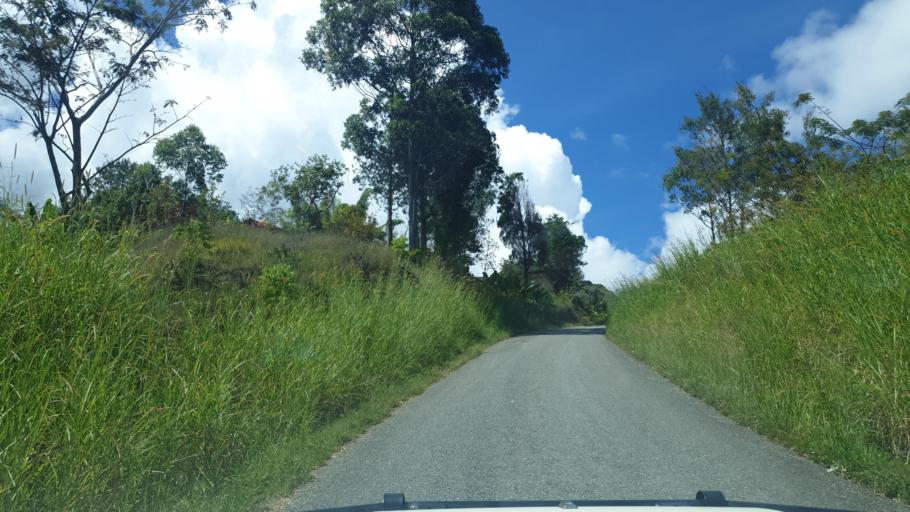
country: PG
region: Chimbu
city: Kundiawa
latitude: -6.1434
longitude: 145.1311
